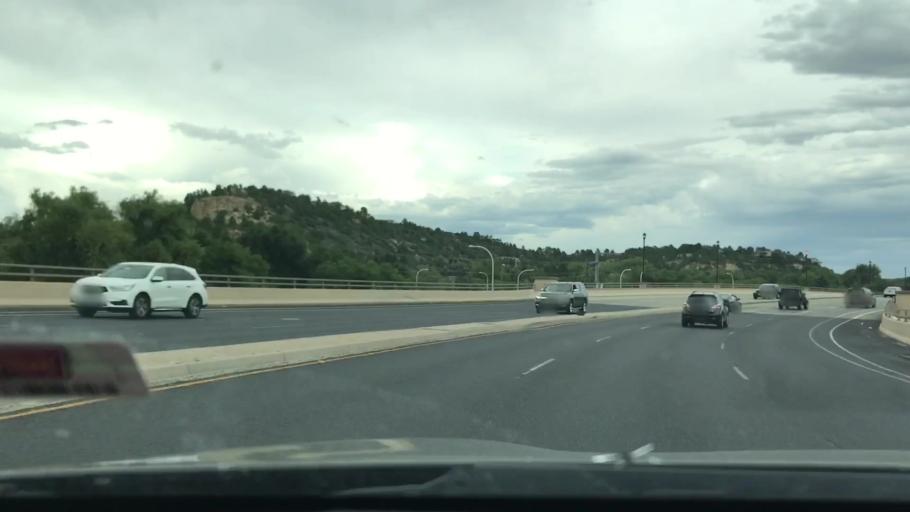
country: US
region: Colorado
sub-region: El Paso County
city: Colorado Springs
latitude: 38.8889
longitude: -104.7872
